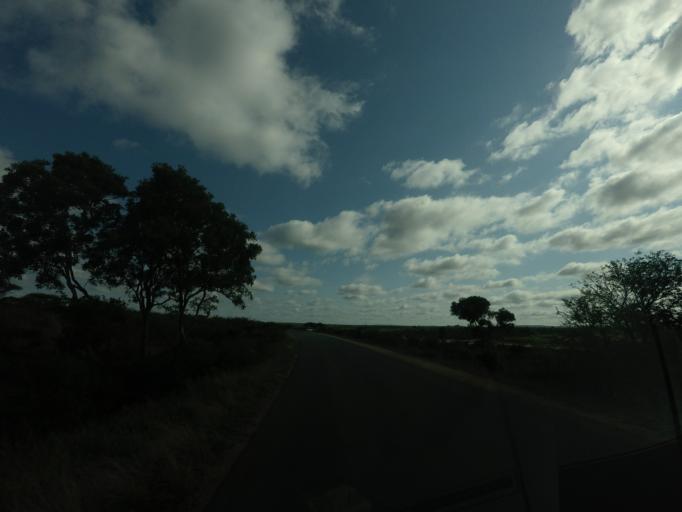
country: ZA
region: Mpumalanga
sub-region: Ehlanzeni District
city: Komatipoort
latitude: -25.1517
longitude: 31.9395
